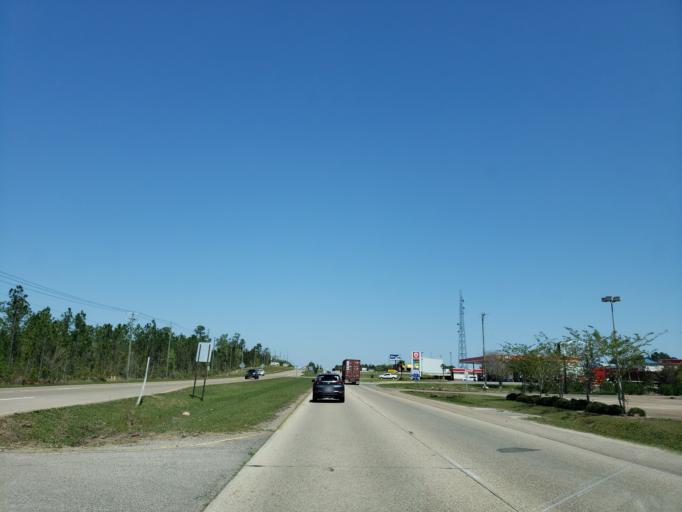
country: US
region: Mississippi
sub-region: Harrison County
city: Lyman
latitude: 30.4838
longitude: -89.1035
